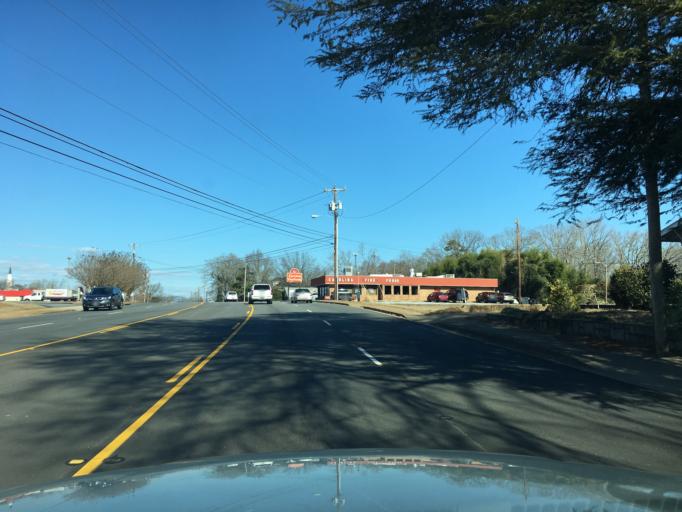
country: US
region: South Carolina
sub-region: Pickens County
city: Pickens
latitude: 34.8797
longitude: -82.7020
